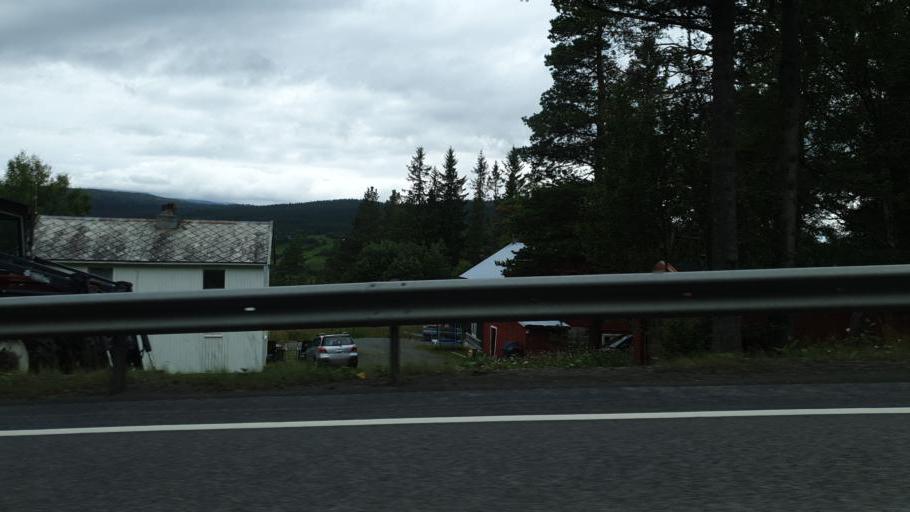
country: NO
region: Sor-Trondelag
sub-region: Rennebu
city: Berkak
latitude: 62.7987
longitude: 10.0236
